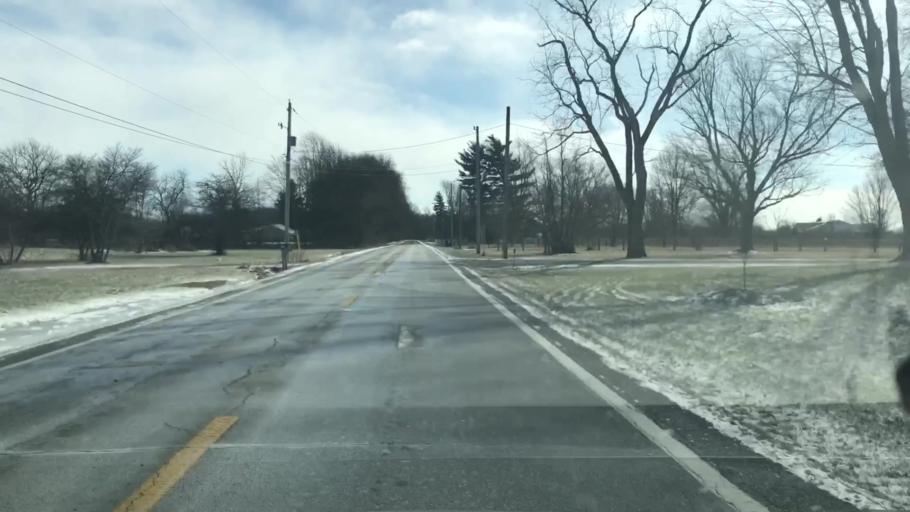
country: US
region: Ohio
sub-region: Franklin County
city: Hilliard
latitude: 40.0230
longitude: -83.2218
